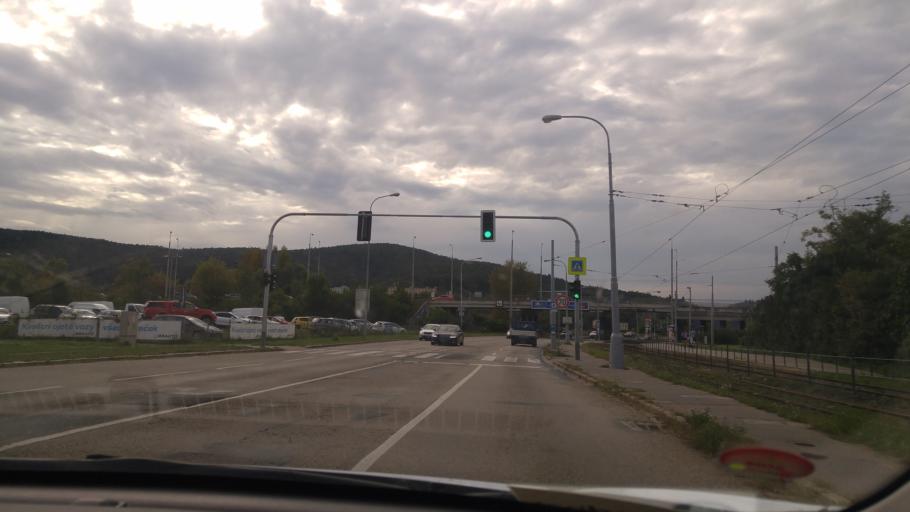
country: CZ
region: South Moravian
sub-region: Mesto Brno
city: Brno
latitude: 49.2128
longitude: 16.5611
